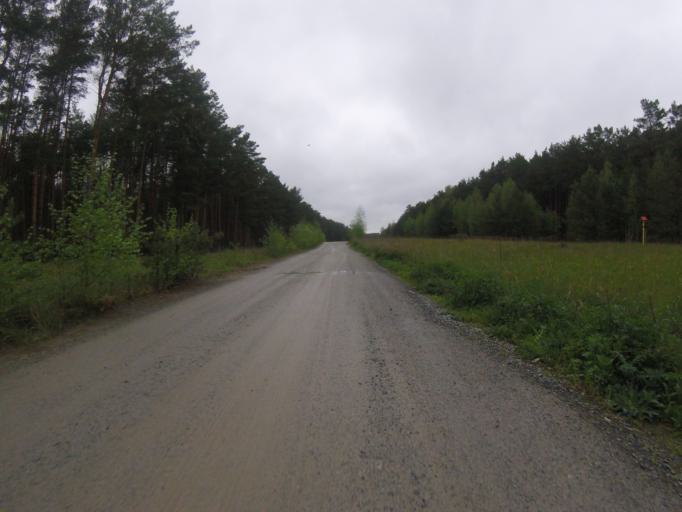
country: DE
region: Brandenburg
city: Schwerin
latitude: 52.1889
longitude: 13.6234
